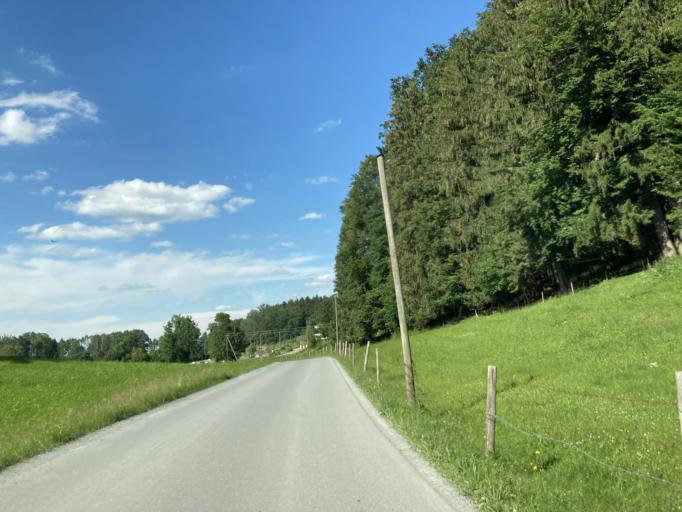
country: DE
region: Bavaria
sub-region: Upper Bavaria
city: Samerberg
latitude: 47.7649
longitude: 12.2283
